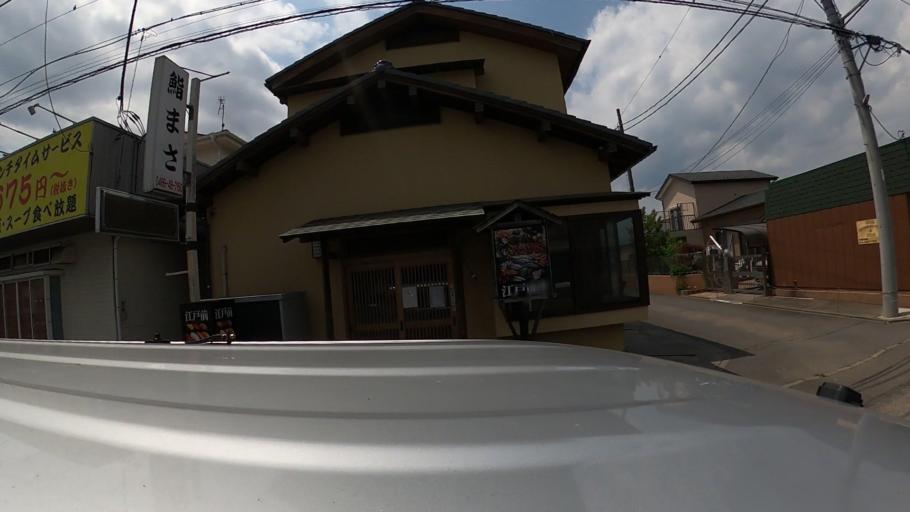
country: JP
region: Kanagawa
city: Chigasaki
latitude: 35.3848
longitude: 139.4017
